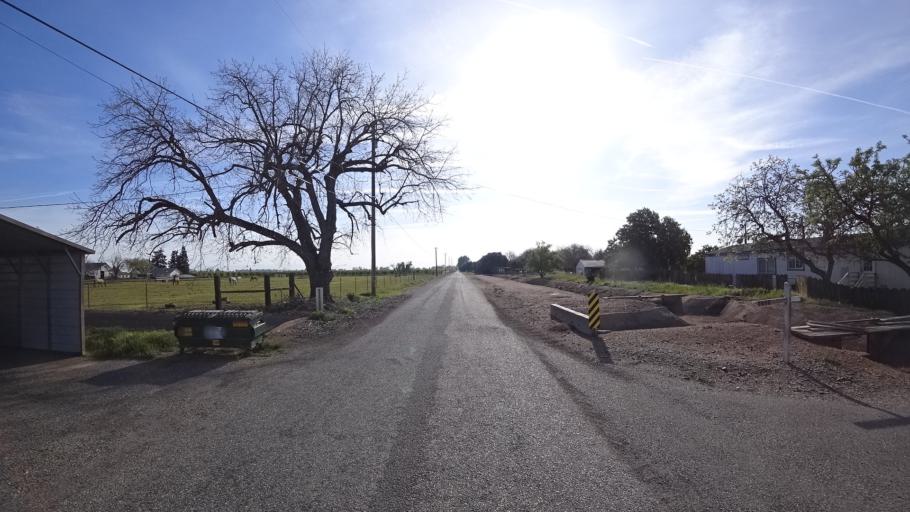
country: US
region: California
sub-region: Glenn County
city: Orland
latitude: 39.7188
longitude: -122.2340
